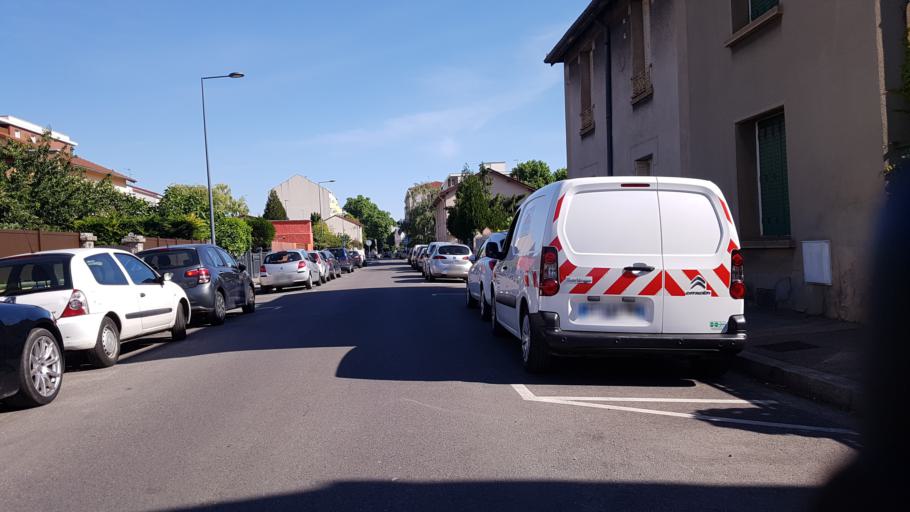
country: FR
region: Rhone-Alpes
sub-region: Departement du Rhone
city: Villeurbanne
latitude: 45.7752
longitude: 4.8844
